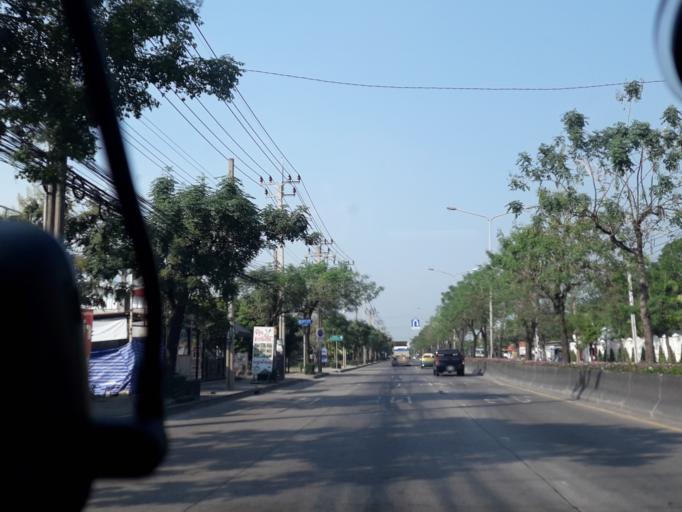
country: TH
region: Bangkok
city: Khlong Sam Wa
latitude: 13.8688
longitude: 100.7318
